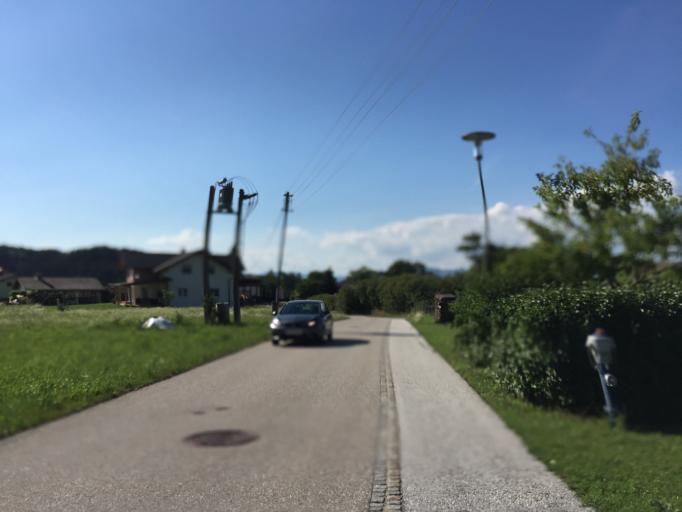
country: AT
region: Carinthia
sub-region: Politischer Bezirk Volkermarkt
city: Feistritz ob Bleiburg
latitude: 46.5590
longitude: 14.7647
